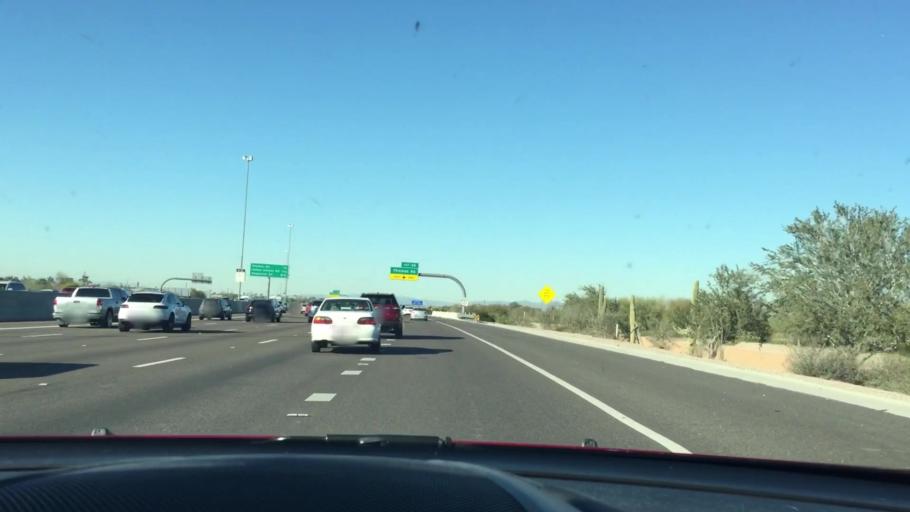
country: US
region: Arizona
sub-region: Maricopa County
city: Scottsdale
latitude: 33.4710
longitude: -111.8903
